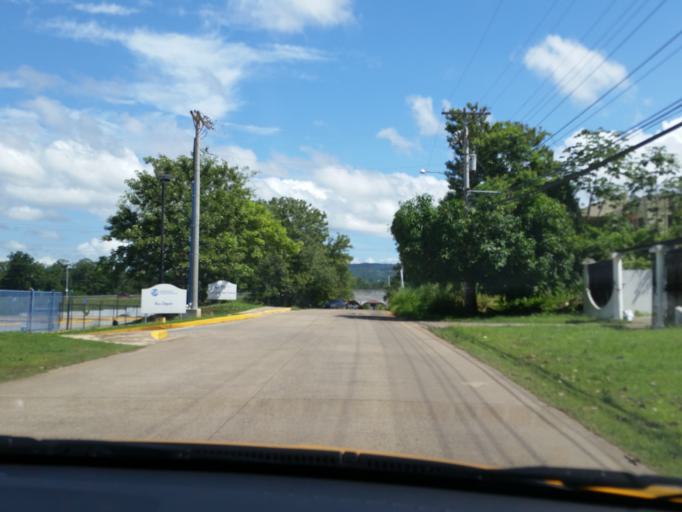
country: PA
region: Panama
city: San Miguelito
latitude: 9.0786
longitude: -79.4705
